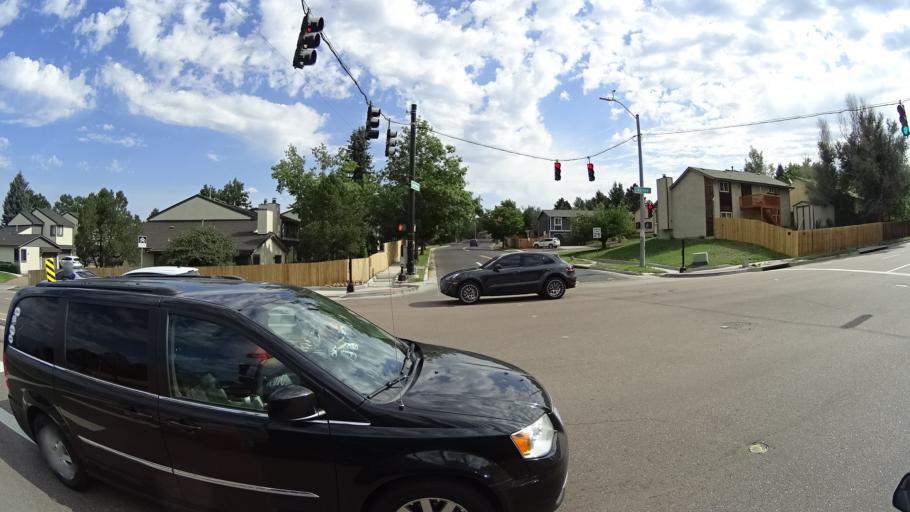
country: US
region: Colorado
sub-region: El Paso County
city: Cimarron Hills
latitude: 38.8962
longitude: -104.7339
